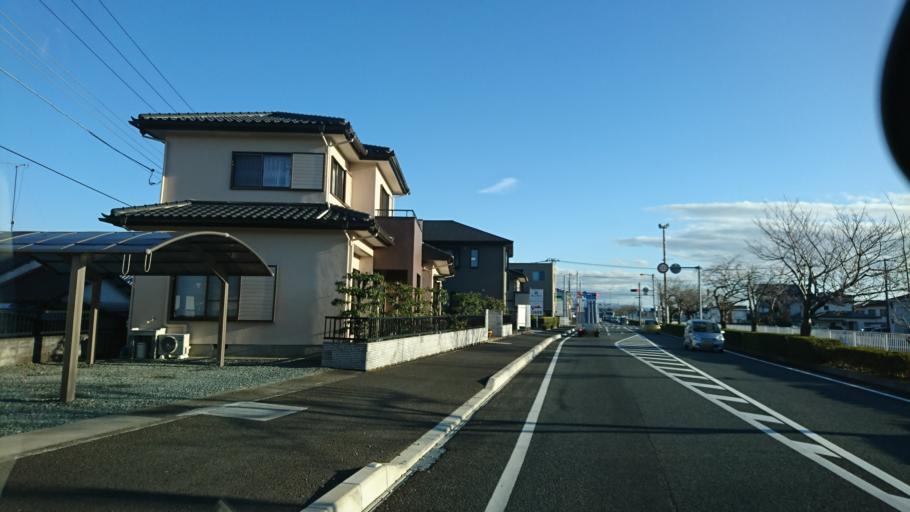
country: JP
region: Shizuoka
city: Fuji
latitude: 35.1371
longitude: 138.6520
